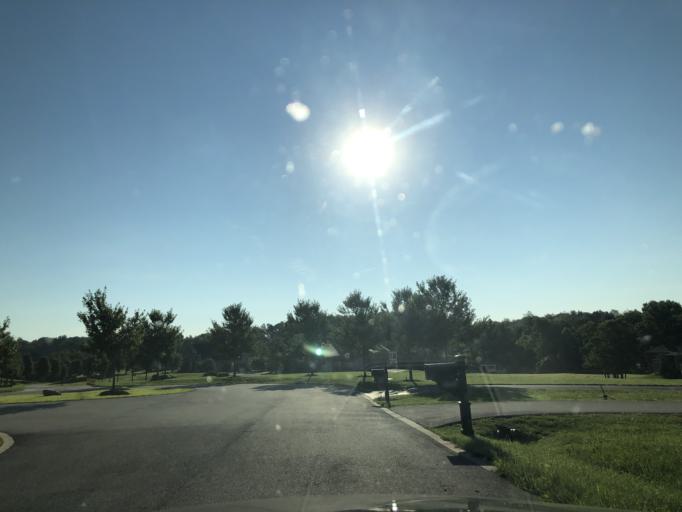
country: US
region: Maryland
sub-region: Howard County
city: Highland
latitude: 39.1939
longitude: -76.9532
